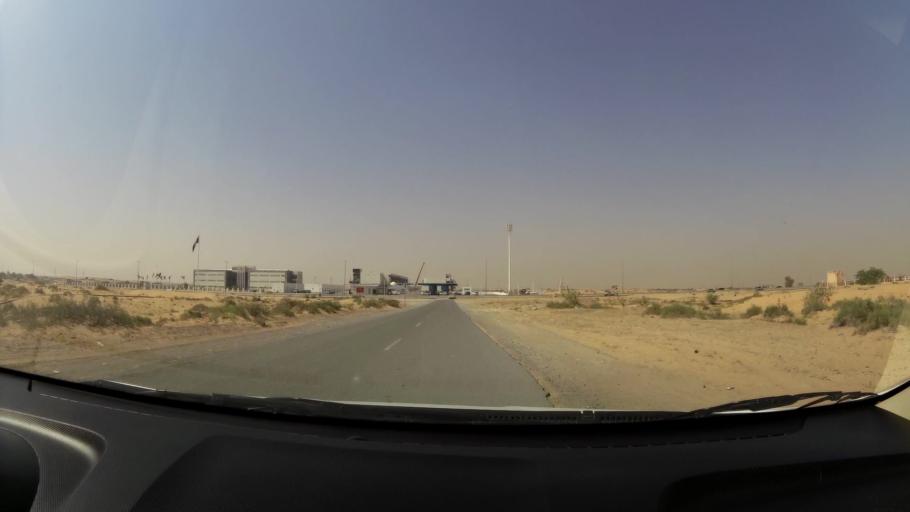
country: AE
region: Ajman
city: Ajman
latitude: 25.3890
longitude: 55.5535
